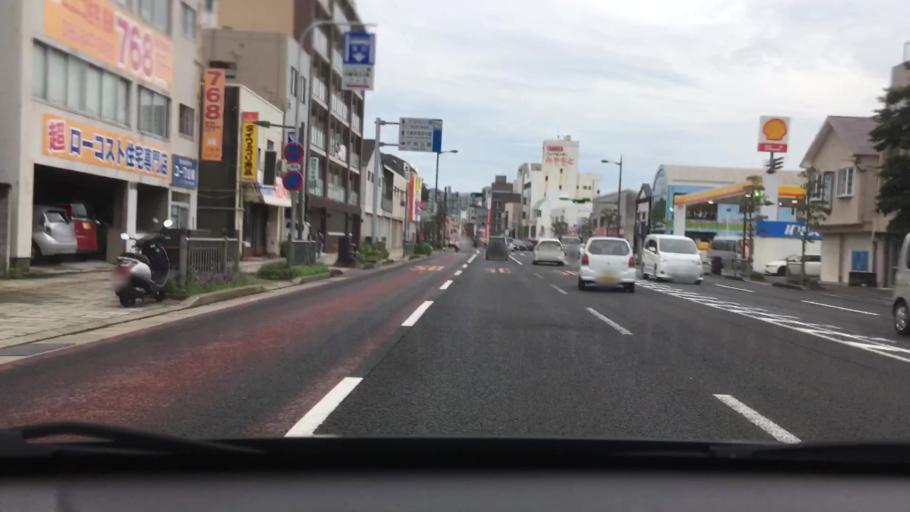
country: JP
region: Nagasaki
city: Nagasaki-shi
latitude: 32.7766
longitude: 129.8620
